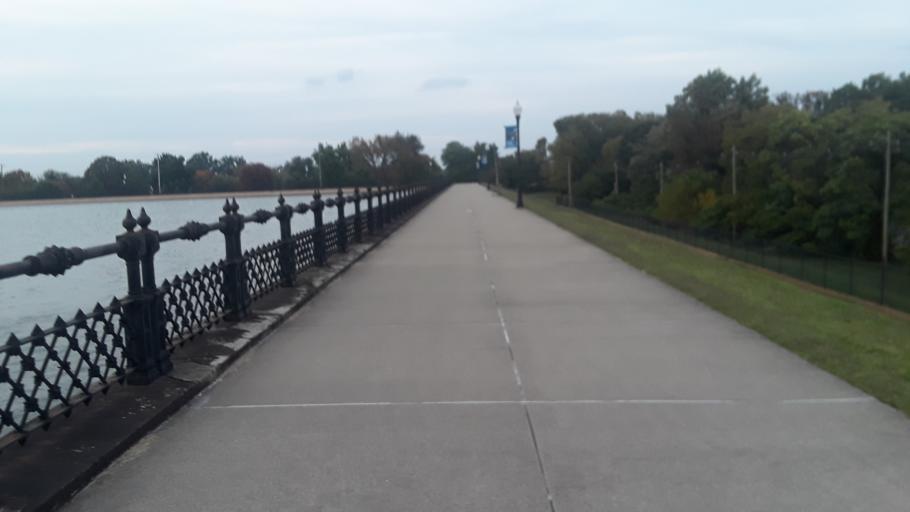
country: US
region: Kentucky
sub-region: Jefferson County
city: Indian Hills
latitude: 38.2571
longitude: -85.6780
